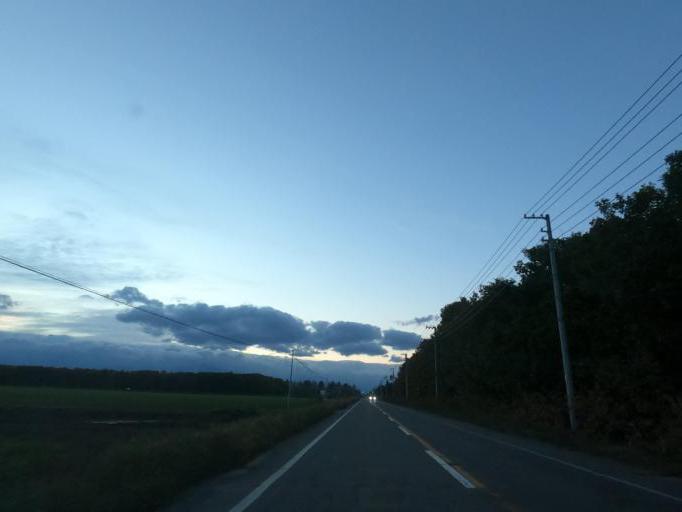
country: JP
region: Hokkaido
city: Obihiro
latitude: 42.6773
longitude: 143.1609
